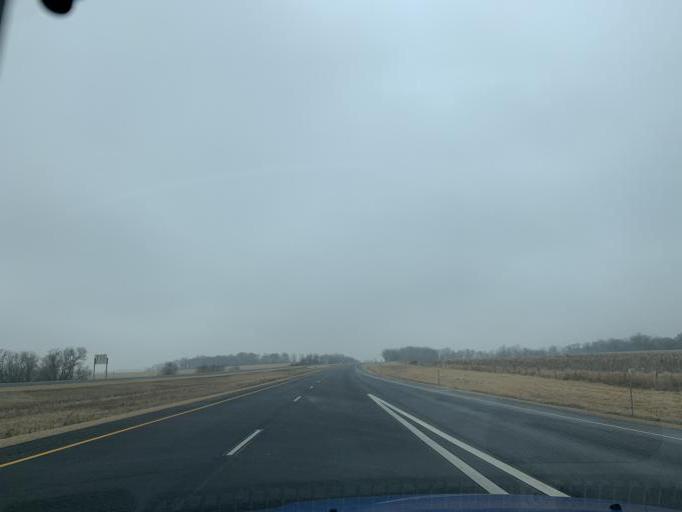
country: US
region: Wisconsin
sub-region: Dane County
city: Sun Prairie
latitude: 43.2440
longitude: -89.1428
